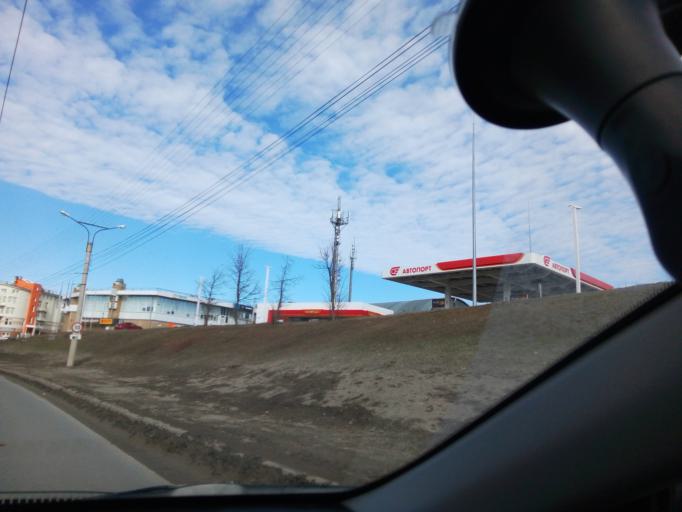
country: RU
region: Chuvashia
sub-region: Cheboksarskiy Rayon
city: Cheboksary
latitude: 56.1155
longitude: 47.2536
